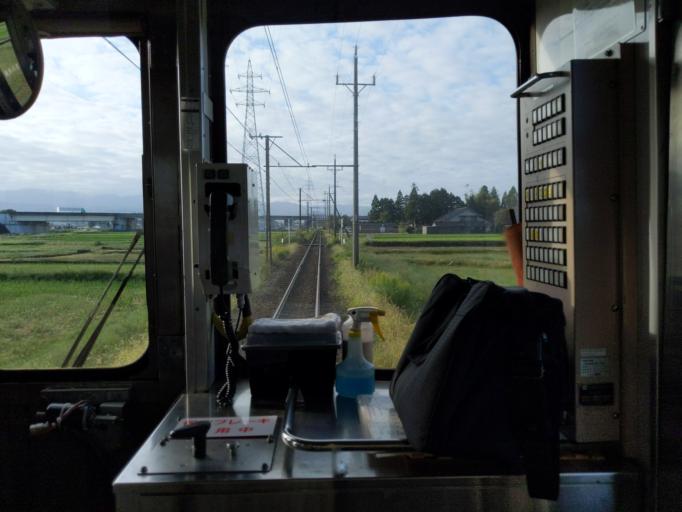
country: JP
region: Toyama
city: Kamiichi
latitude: 36.6820
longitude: 137.3177
